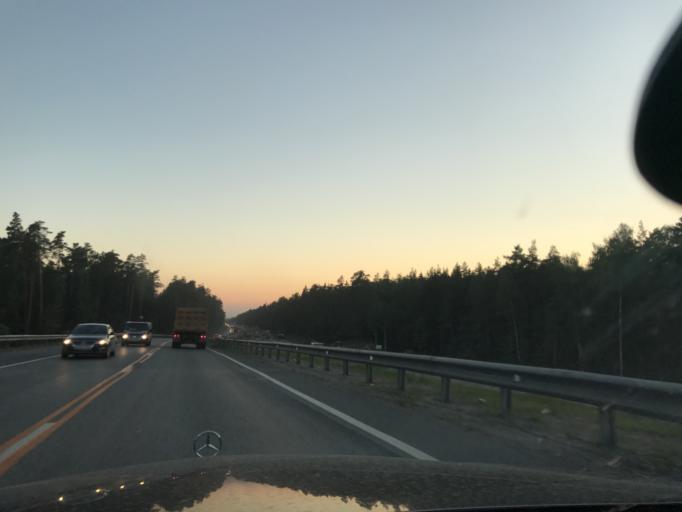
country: RU
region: Moskovskaya
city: Malaya Dubna
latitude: 55.8845
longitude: 39.0008
